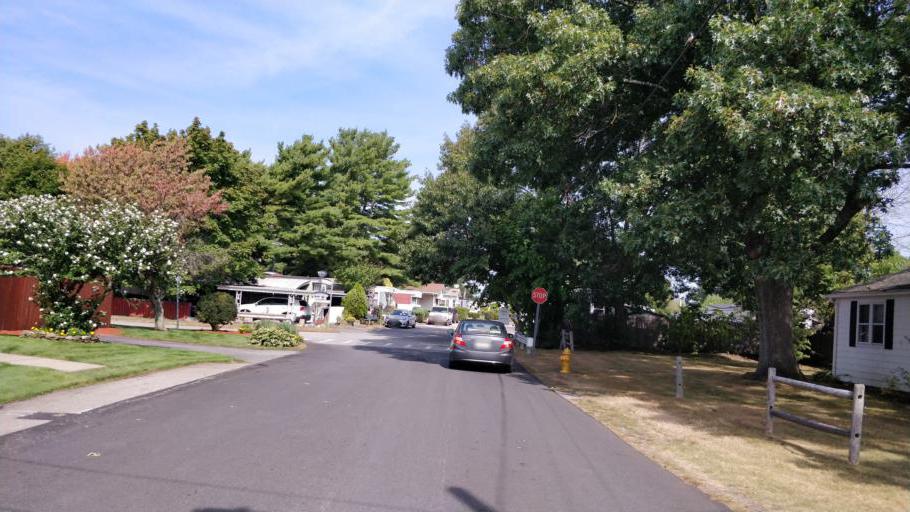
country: US
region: Massachusetts
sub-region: Bristol County
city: North Seekonk
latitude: 41.8967
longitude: -71.3511
